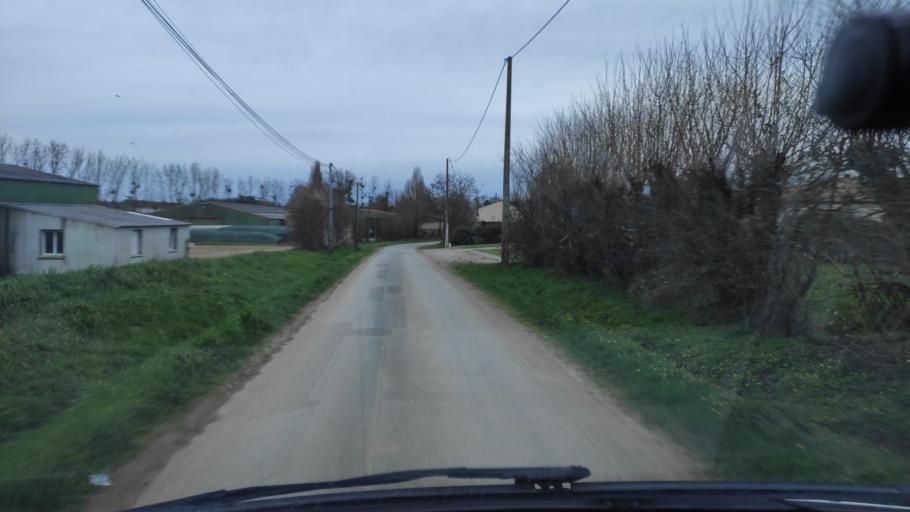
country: FR
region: Pays de la Loire
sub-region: Departement de la Vendee
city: Saint-Andre-Treize-Voies
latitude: 46.8971
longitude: -1.4312
